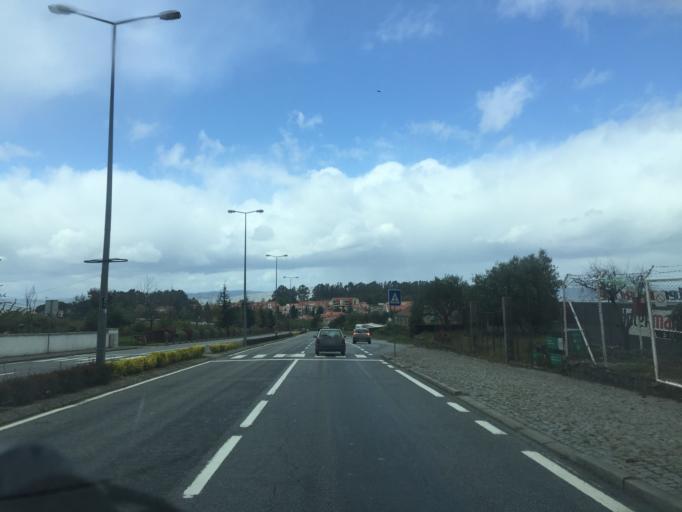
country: PT
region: Guarda
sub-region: Manteigas
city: Manteigas
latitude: 40.4980
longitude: -7.6035
